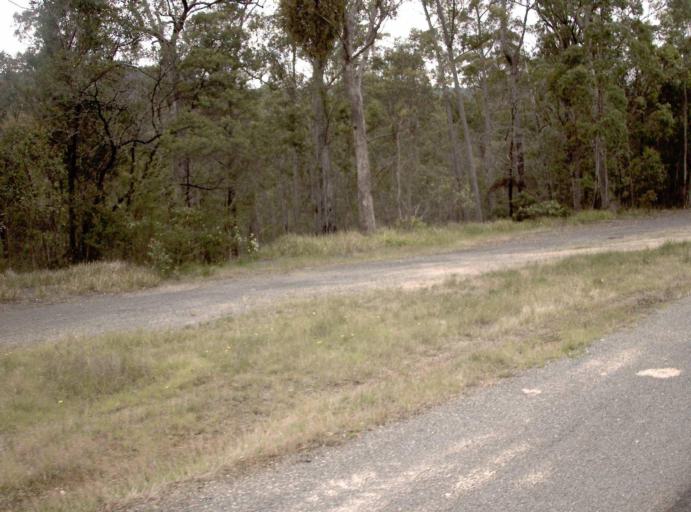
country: AU
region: New South Wales
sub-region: Bombala
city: Bombala
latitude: -37.2783
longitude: 149.2239
